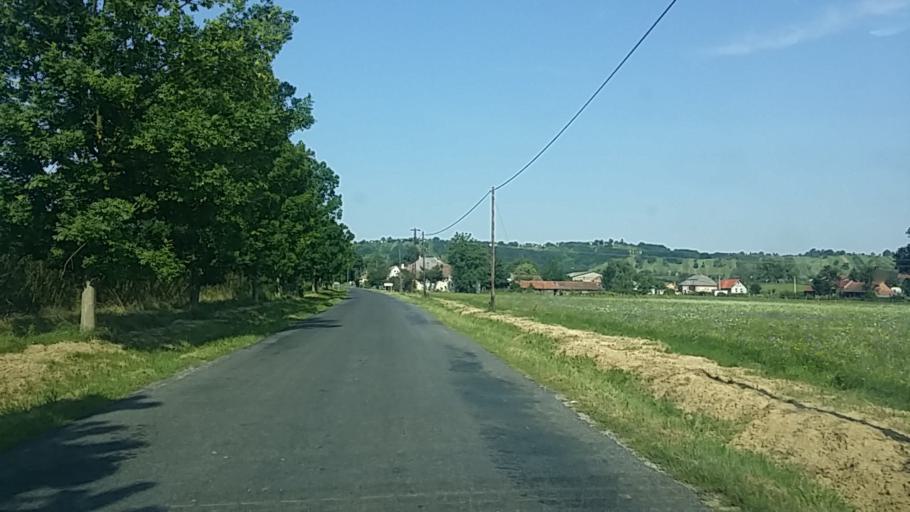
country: HU
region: Zala
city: Lenti
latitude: 46.5728
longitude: 16.5746
